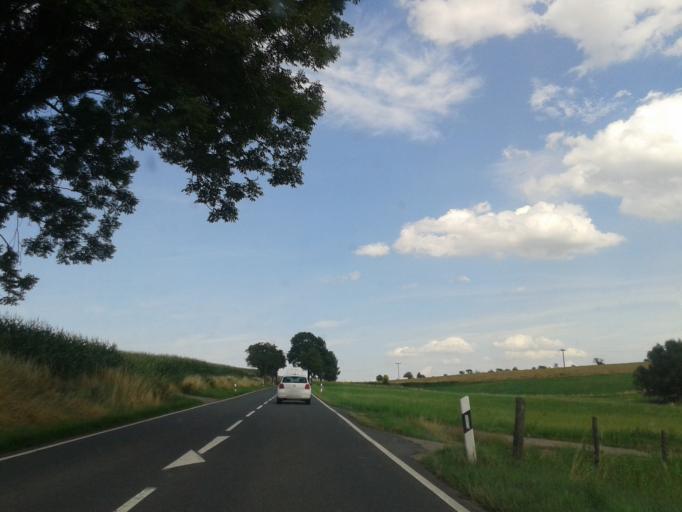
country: DE
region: Saxony
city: Niederschona
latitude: 51.0478
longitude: 13.4404
